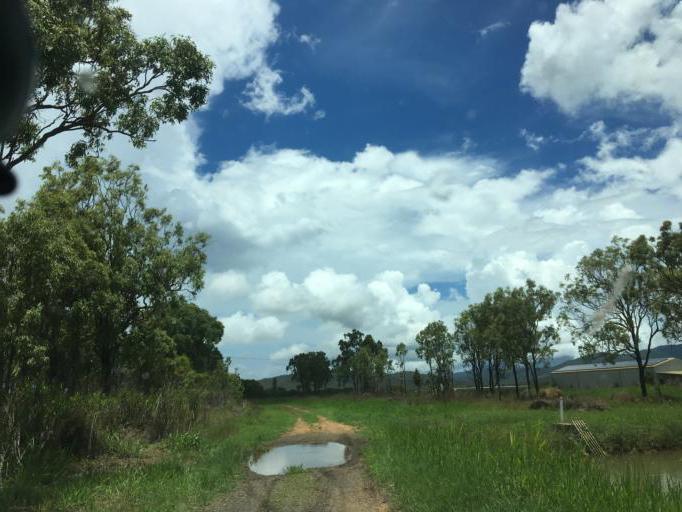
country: AU
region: Queensland
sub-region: Tablelands
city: Mareeba
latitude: -16.9885
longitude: 145.5258
